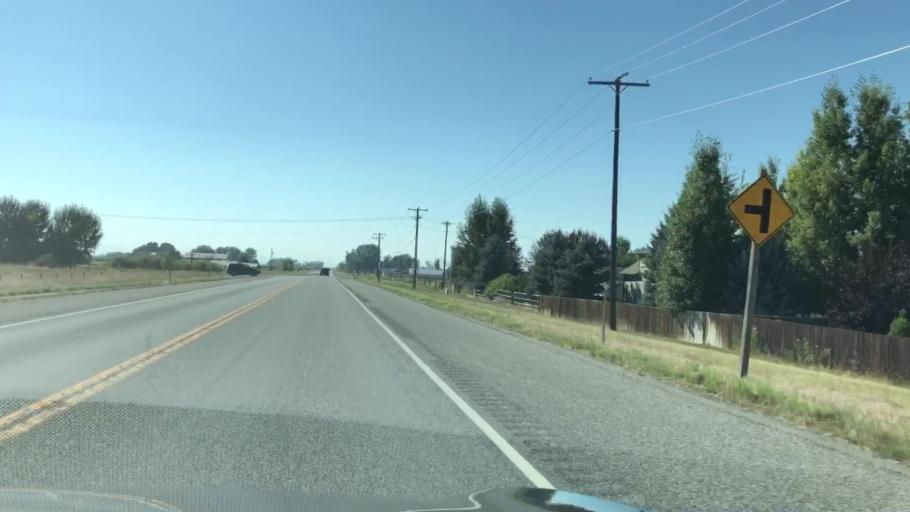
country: US
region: Montana
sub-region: Gallatin County
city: Belgrade
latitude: 45.7294
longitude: -111.1435
